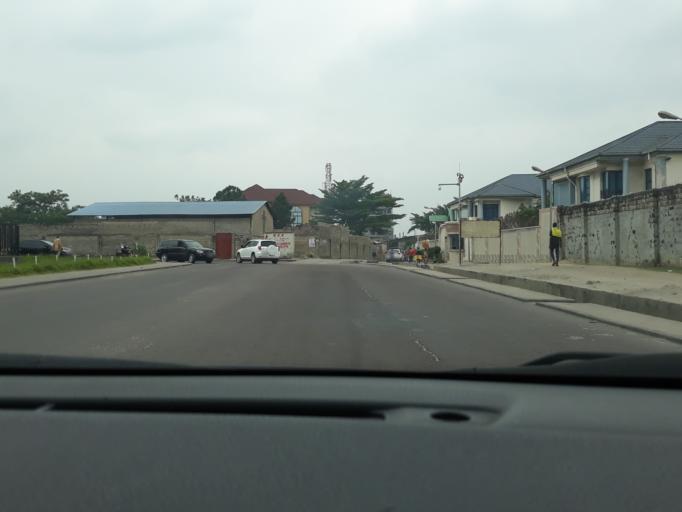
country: CD
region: Kinshasa
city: Kinshasa
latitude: -4.3305
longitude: 15.3052
